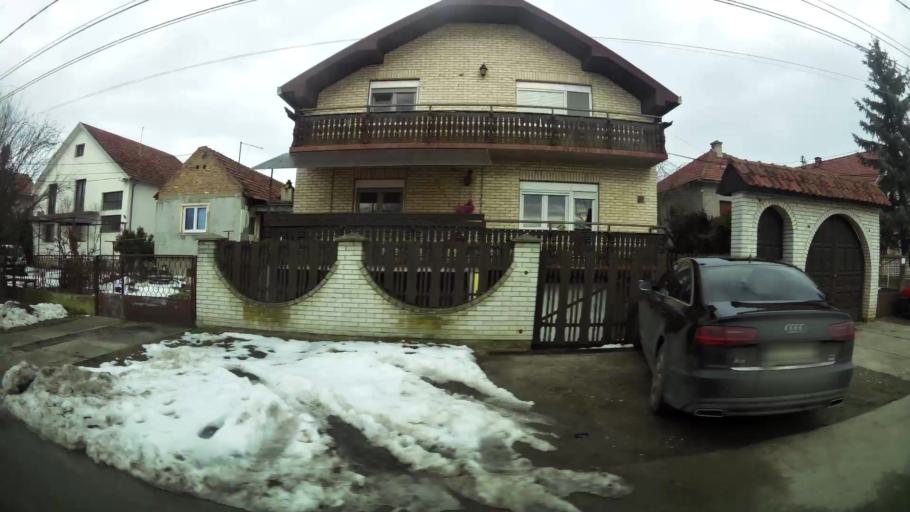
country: RS
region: Central Serbia
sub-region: Belgrade
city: Surcin
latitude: 44.7999
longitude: 20.2859
